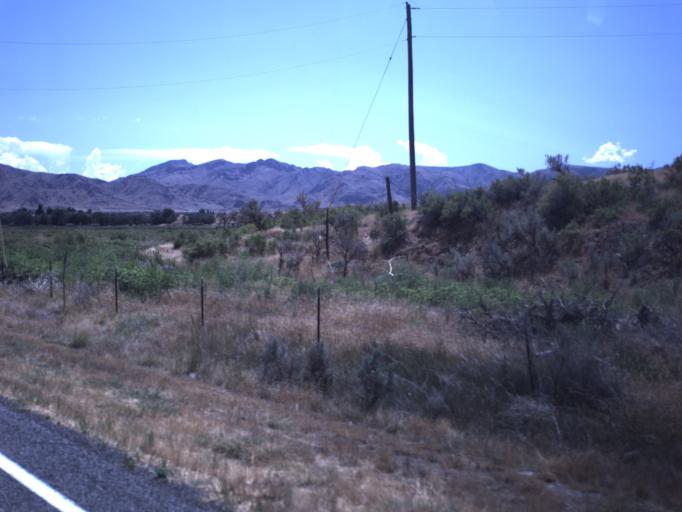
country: US
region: Utah
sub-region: Millard County
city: Delta
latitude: 39.5334
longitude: -112.3136
